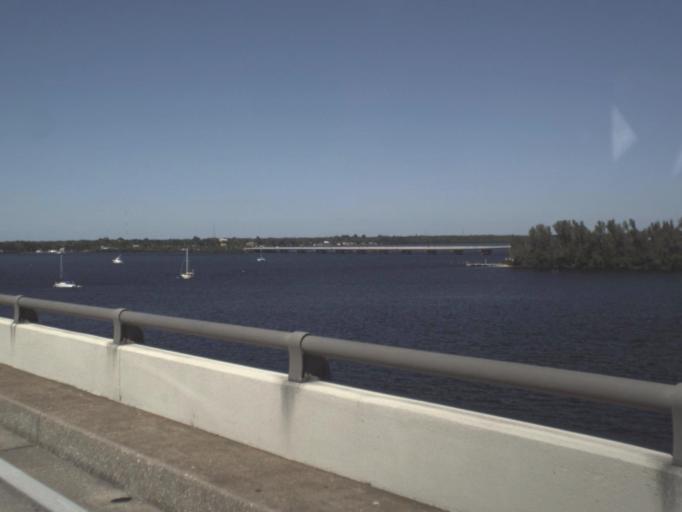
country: US
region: Florida
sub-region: Lee County
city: North Fort Myers
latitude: 26.6460
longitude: -81.8749
